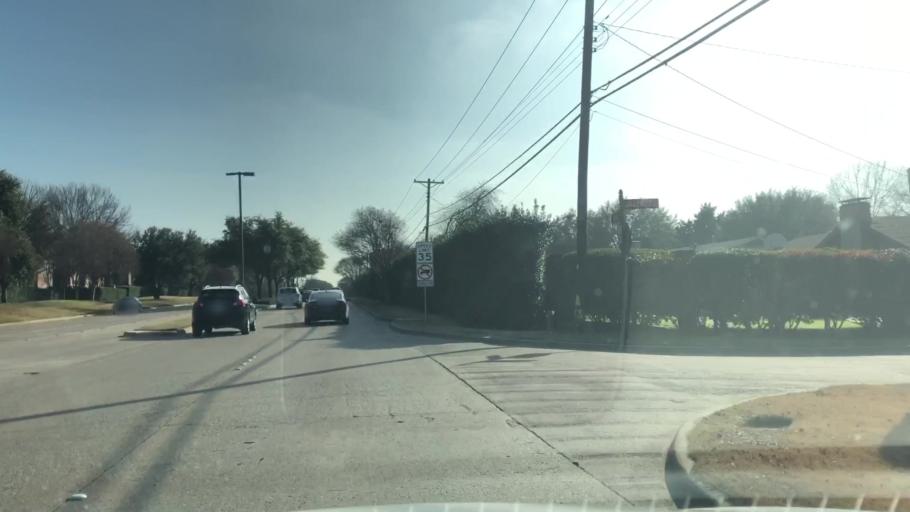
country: US
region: Texas
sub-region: Dallas County
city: Addison
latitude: 32.9472
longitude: -96.8558
